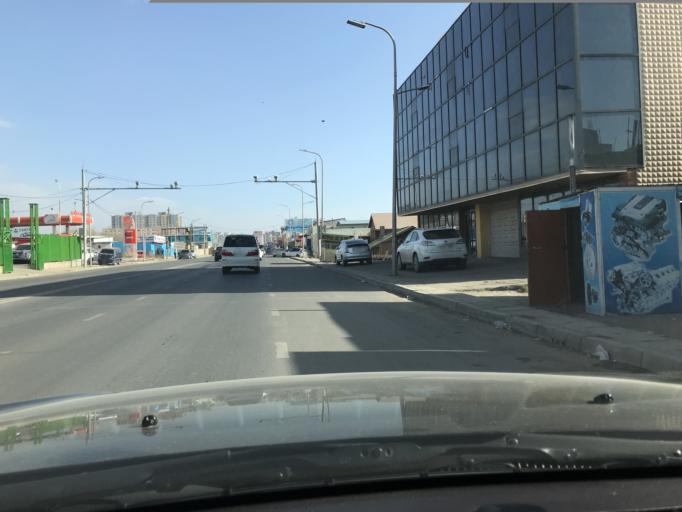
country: MN
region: Ulaanbaatar
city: Ulaanbaatar
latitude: 47.9235
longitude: 106.9572
